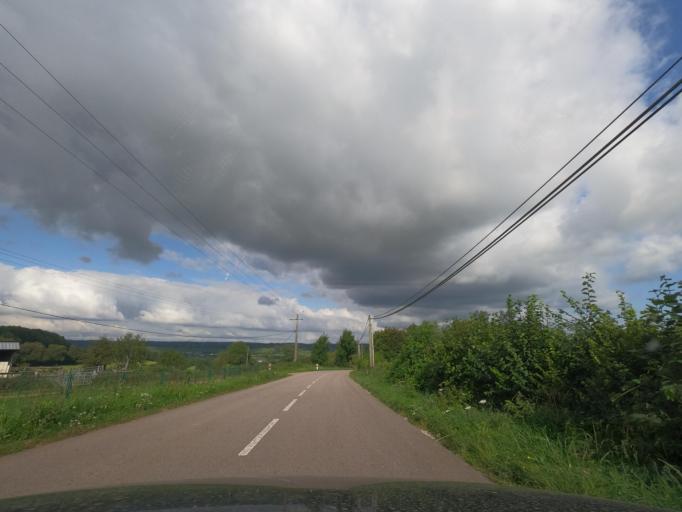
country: FR
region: Lower Normandy
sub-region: Departement de l'Orne
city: Gace
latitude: 48.7913
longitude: 0.2744
